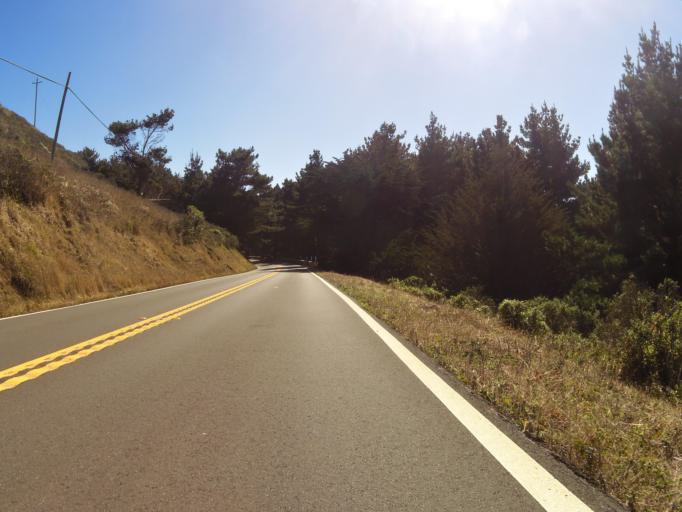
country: US
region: California
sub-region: Mendocino County
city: Fort Bragg
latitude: 39.6024
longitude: -123.7855
